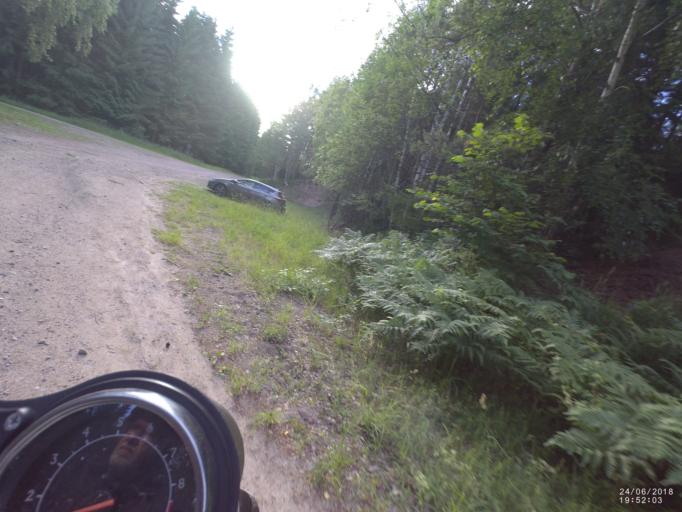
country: SE
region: Soedermanland
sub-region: Oxelosunds Kommun
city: Oxelosund
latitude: 58.7716
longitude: 17.1544
